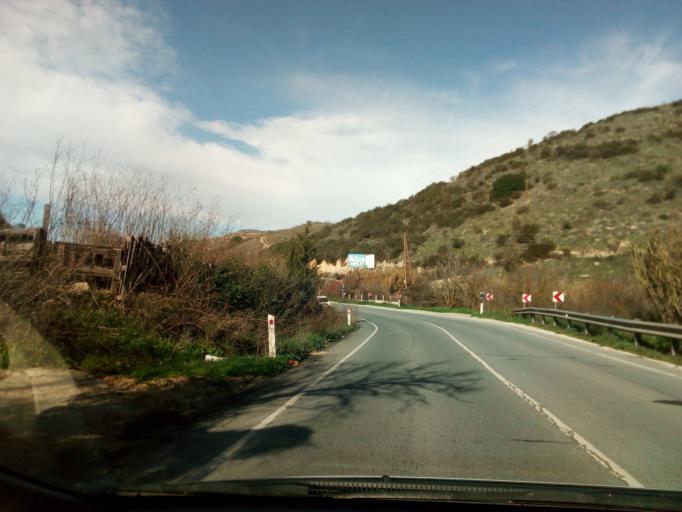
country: CY
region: Pafos
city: Tala
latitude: 34.8687
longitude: 32.4833
